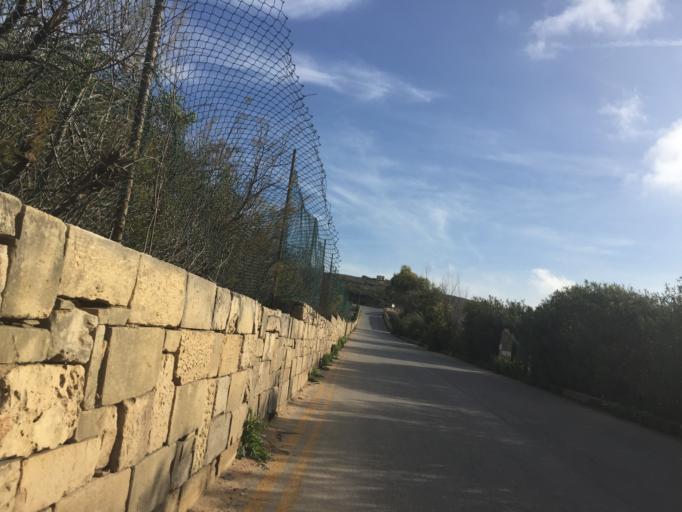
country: MT
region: L-Imgarr
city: Imgarr
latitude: 35.9324
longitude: 14.3467
